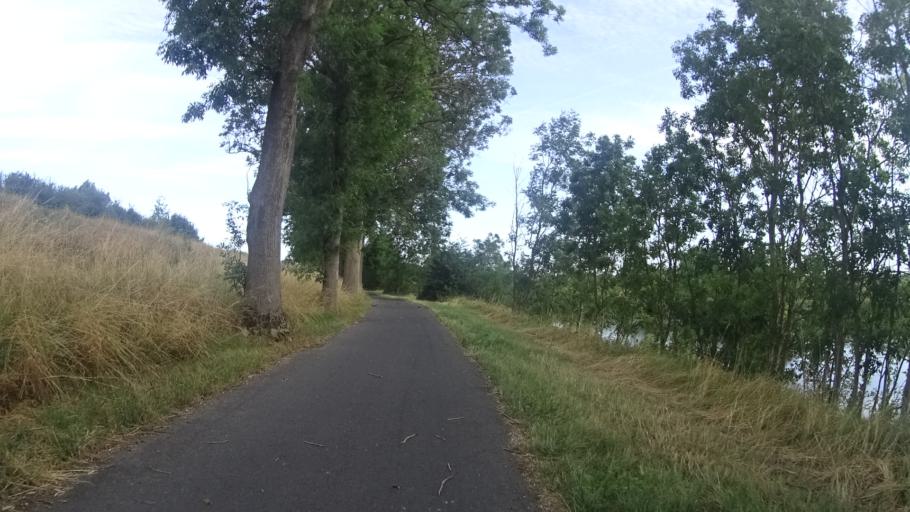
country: BE
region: Flanders
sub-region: Provincie West-Vlaanderen
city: Ieper
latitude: 50.9174
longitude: 2.8468
